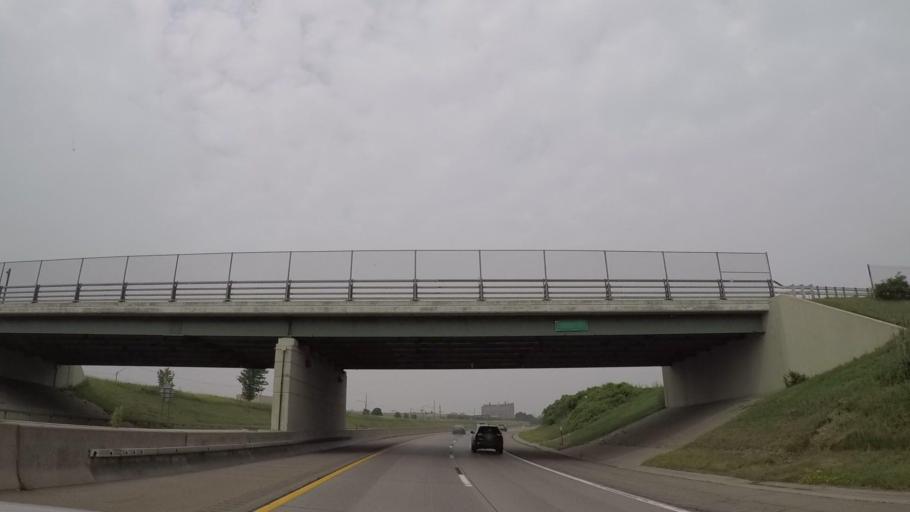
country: US
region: New York
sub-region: Erie County
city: Grandyle Village
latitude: 42.9660
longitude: -78.9208
